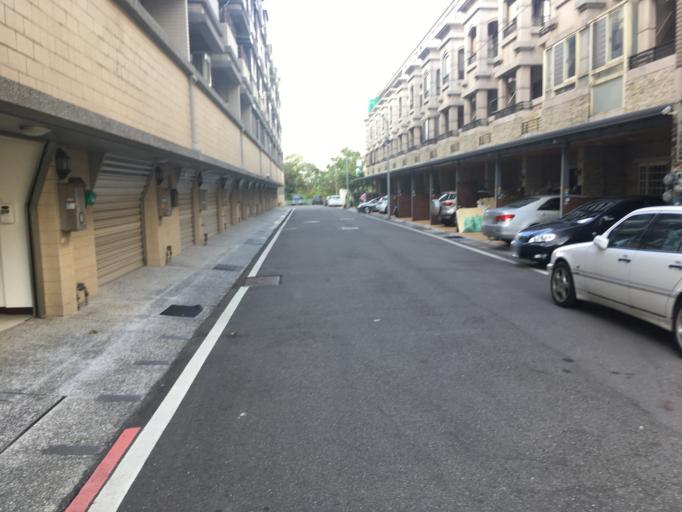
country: TW
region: Taiwan
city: Daxi
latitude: 24.9007
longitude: 121.1486
